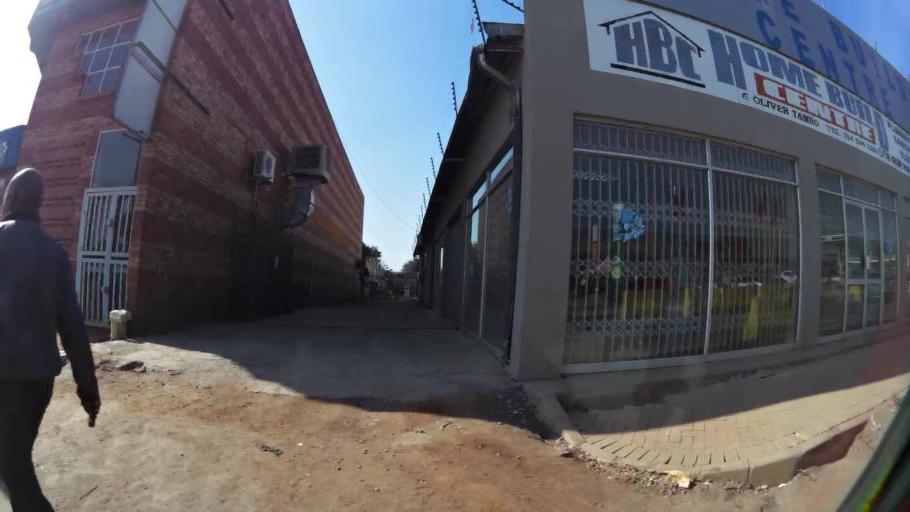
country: ZA
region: North-West
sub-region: Bojanala Platinum District Municipality
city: Rustenburg
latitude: -25.6633
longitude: 27.2408
